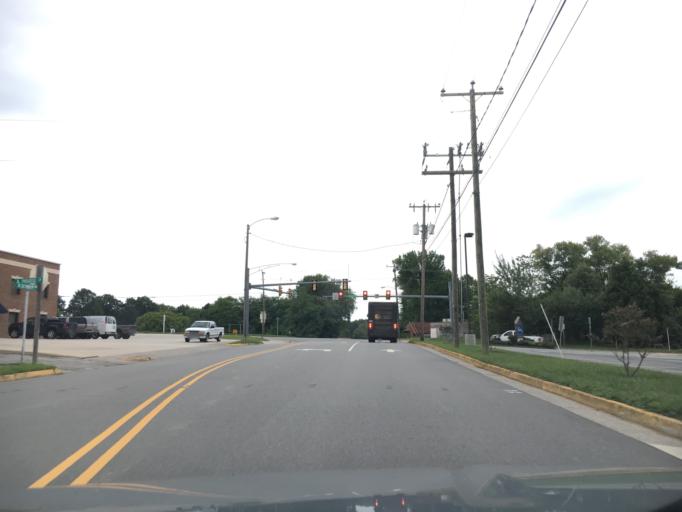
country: US
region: Virginia
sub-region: Halifax County
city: South Boston
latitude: 36.6962
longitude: -78.9005
